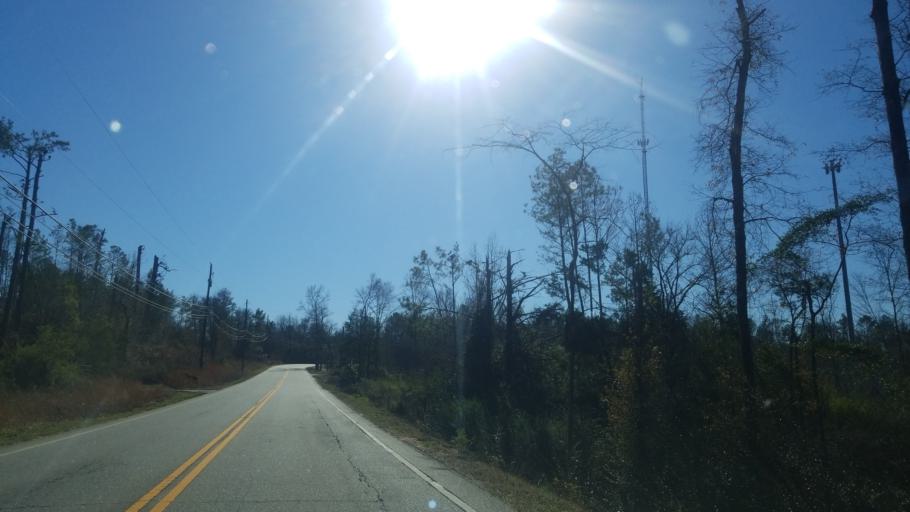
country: US
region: Alabama
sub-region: Lee County
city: Smiths Station
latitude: 32.5813
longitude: -85.0183
